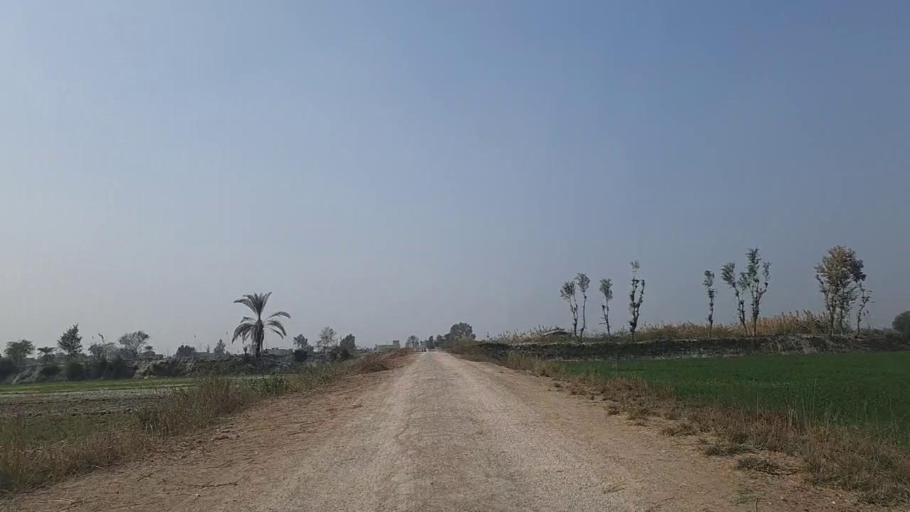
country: PK
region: Sindh
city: Daur
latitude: 26.4488
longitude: 68.4464
